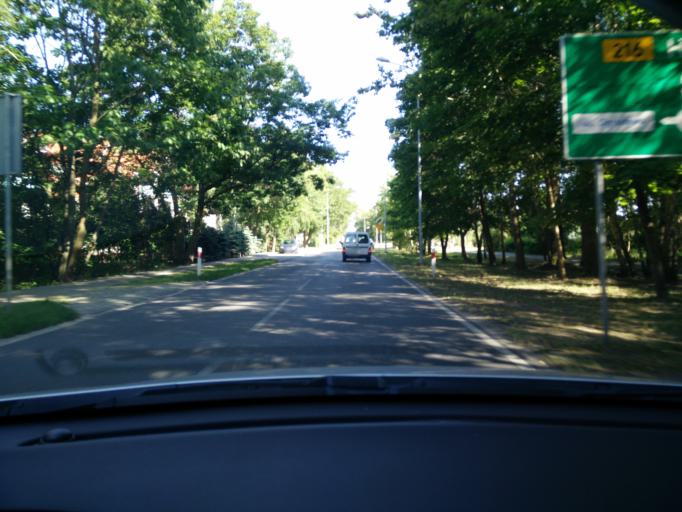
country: PL
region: Pomeranian Voivodeship
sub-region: Powiat pucki
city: Jastarnia
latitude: 54.7070
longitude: 18.6560
